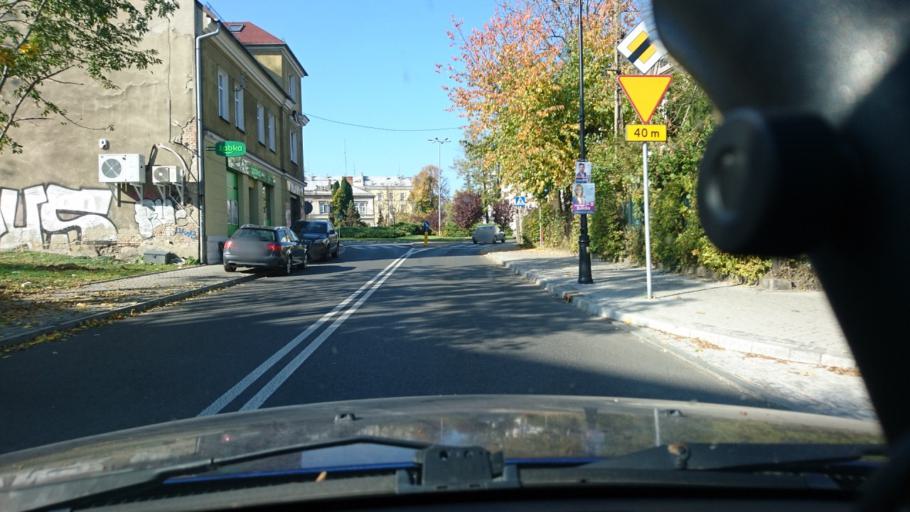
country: PL
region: Silesian Voivodeship
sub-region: Bielsko-Biala
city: Bielsko-Biala
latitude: 49.8204
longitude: 19.0317
